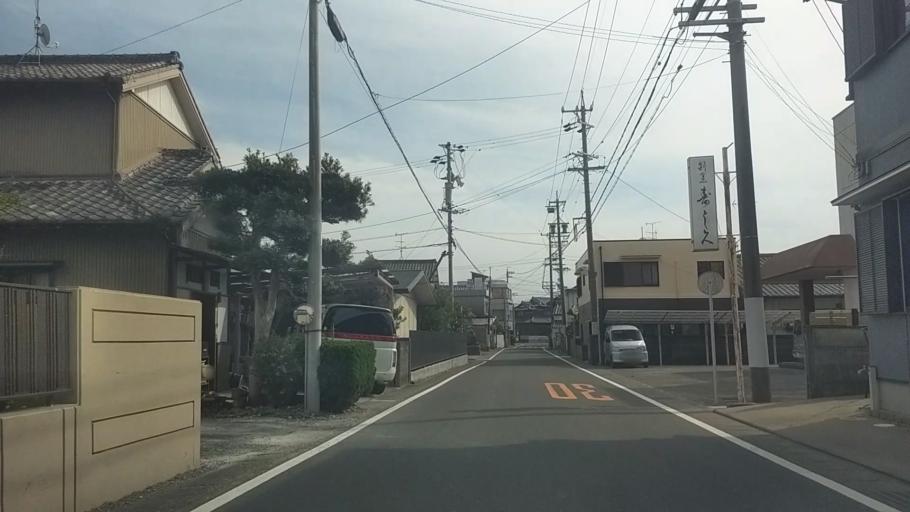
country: JP
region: Shizuoka
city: Kosai-shi
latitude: 34.6992
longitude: 137.6286
